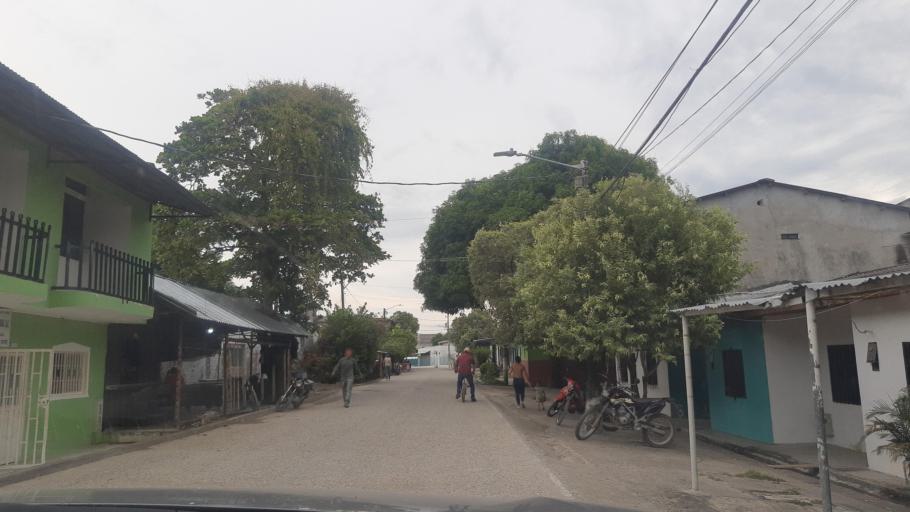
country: CO
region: Antioquia
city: Puerto Triunfo
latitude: 5.8734
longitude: -74.6395
